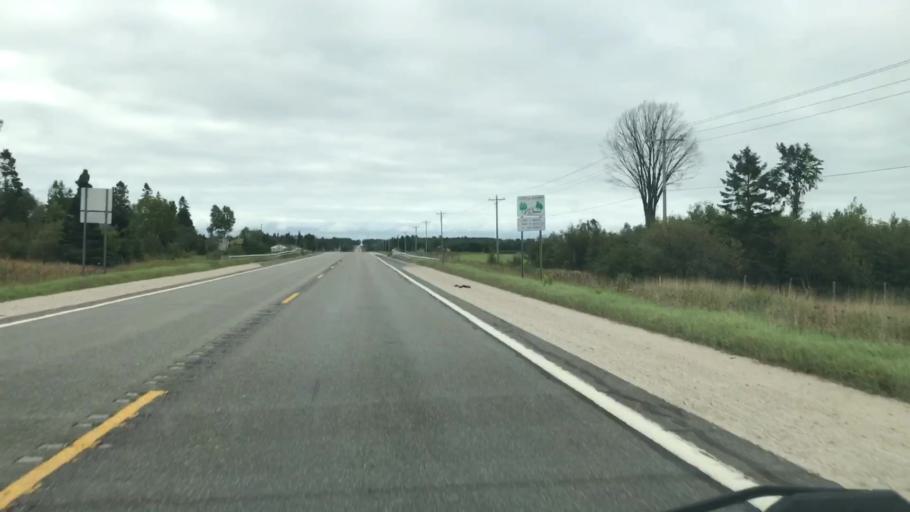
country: US
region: Michigan
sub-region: Luce County
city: Newberry
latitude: 46.1488
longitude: -85.5714
